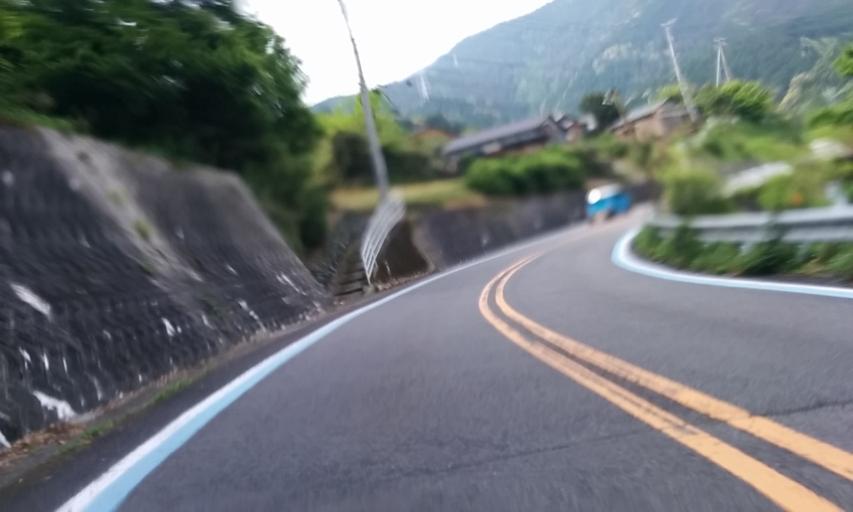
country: JP
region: Ehime
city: Niihama
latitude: 33.9106
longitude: 133.3099
